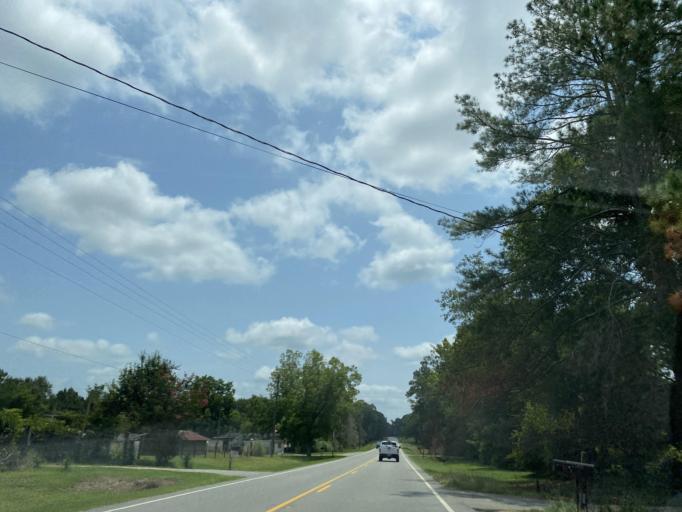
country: US
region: Georgia
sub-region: Jeff Davis County
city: Hazlehurst
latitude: 31.7806
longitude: -82.5631
